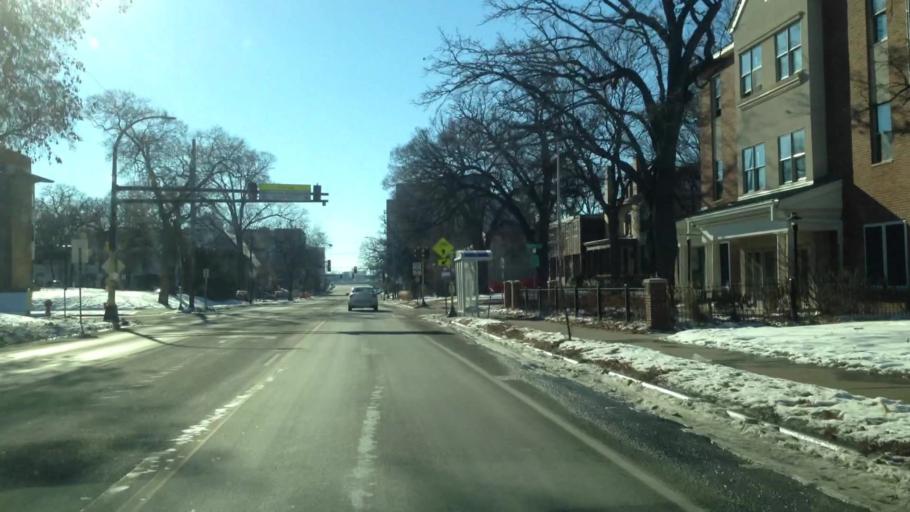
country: US
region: Minnesota
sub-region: Hennepin County
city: Minneapolis
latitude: 44.9841
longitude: -93.2403
